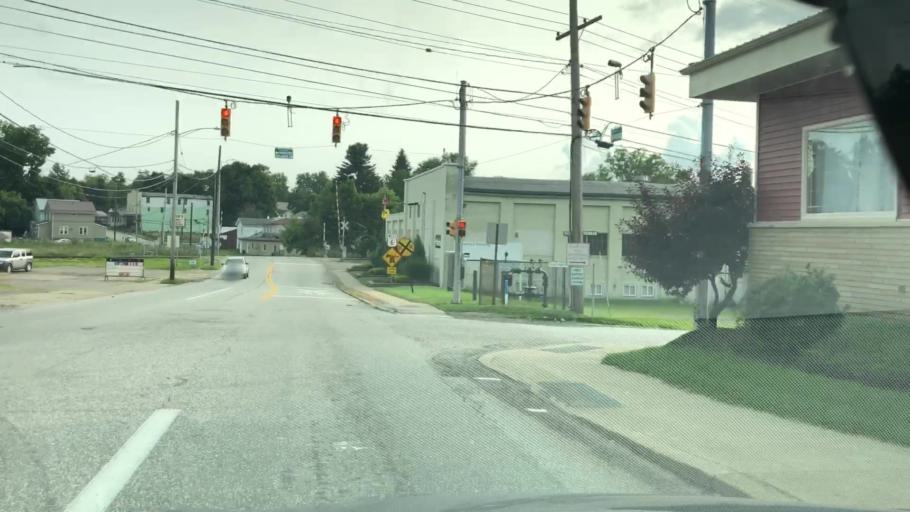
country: US
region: Pennsylvania
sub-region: Erie County
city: Union City
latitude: 41.8962
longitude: -79.8476
